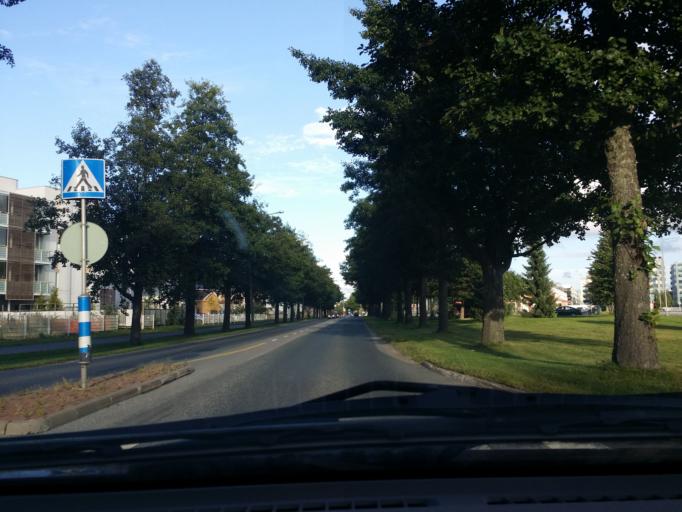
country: FI
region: Satakunta
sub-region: Pori
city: Pori
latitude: 61.4889
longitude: 21.7740
